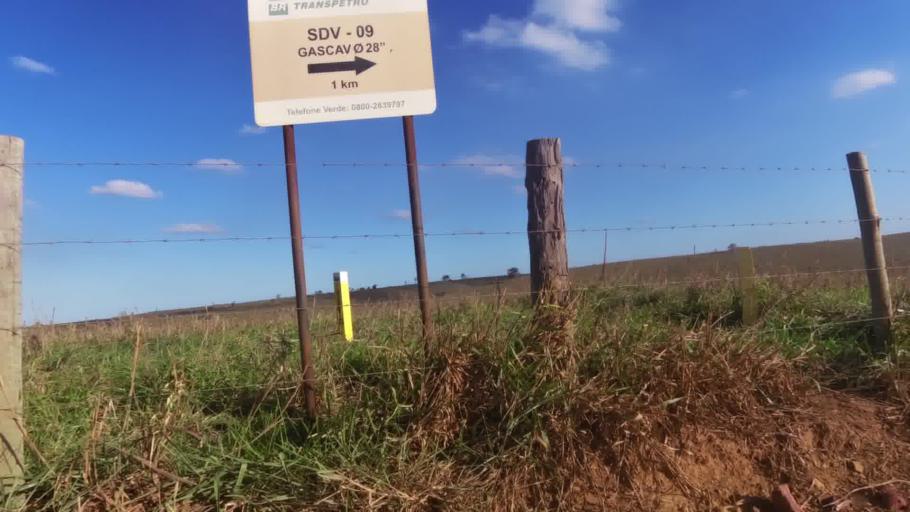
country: BR
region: Espirito Santo
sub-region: Marataizes
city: Marataizes
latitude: -21.1413
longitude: -41.0589
